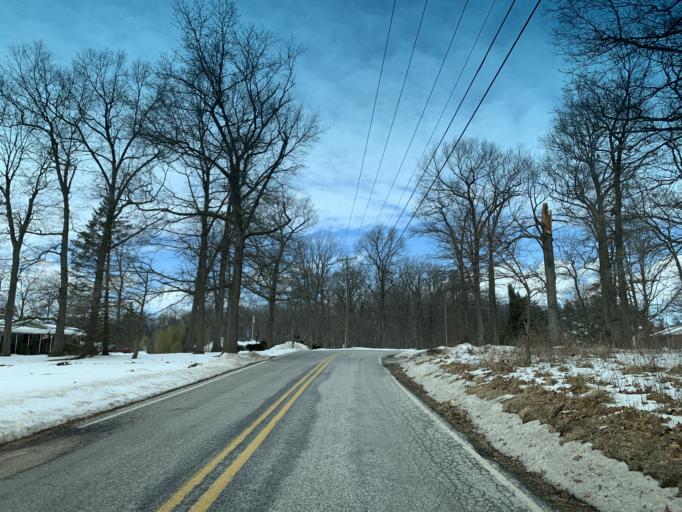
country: US
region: Pennsylvania
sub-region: York County
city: Stewartstown
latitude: 39.7763
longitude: -76.6327
